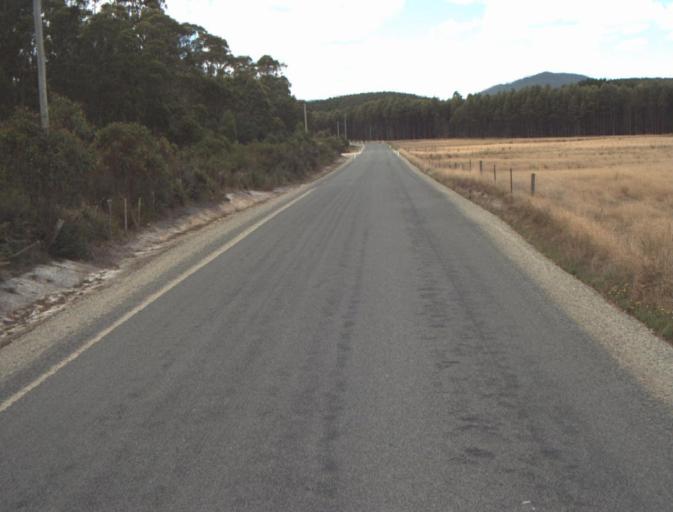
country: AU
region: Tasmania
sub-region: Launceston
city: Mayfield
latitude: -41.2102
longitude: 147.1885
